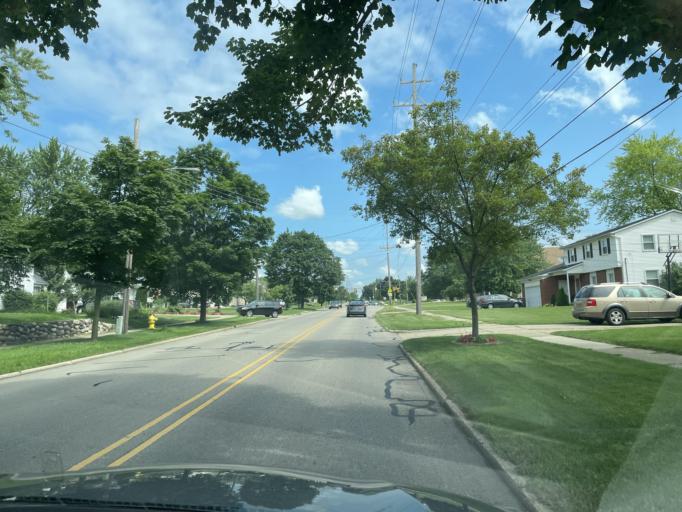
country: US
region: Michigan
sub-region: Kent County
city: East Grand Rapids
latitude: 42.9252
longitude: -85.6237
